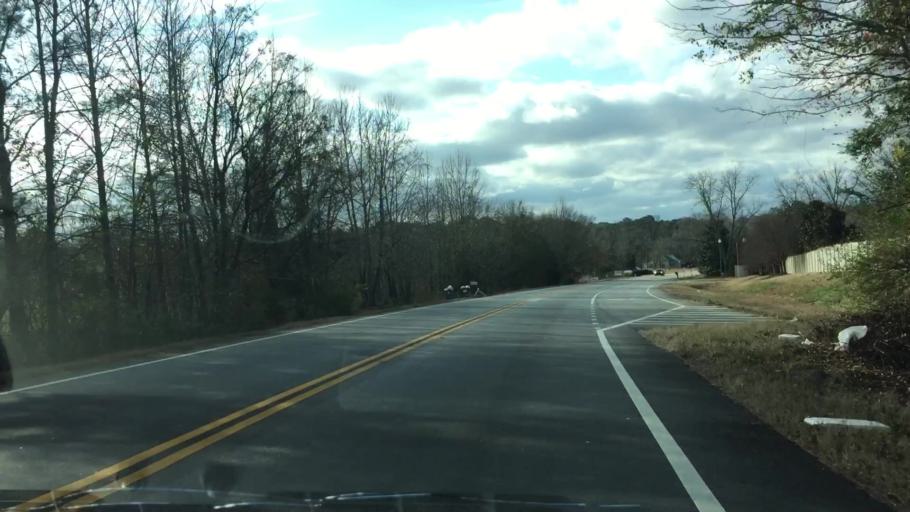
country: US
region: Georgia
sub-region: Henry County
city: McDonough
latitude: 33.4270
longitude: -84.0776
